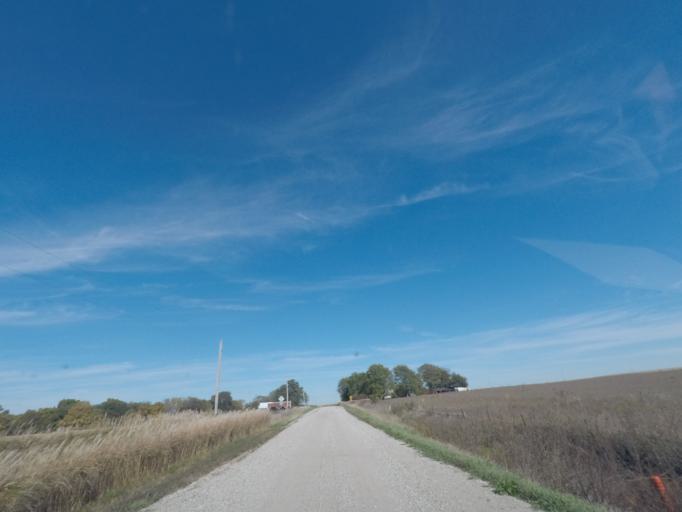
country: US
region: Iowa
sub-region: Story County
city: Nevada
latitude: 42.0424
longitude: -93.3596
